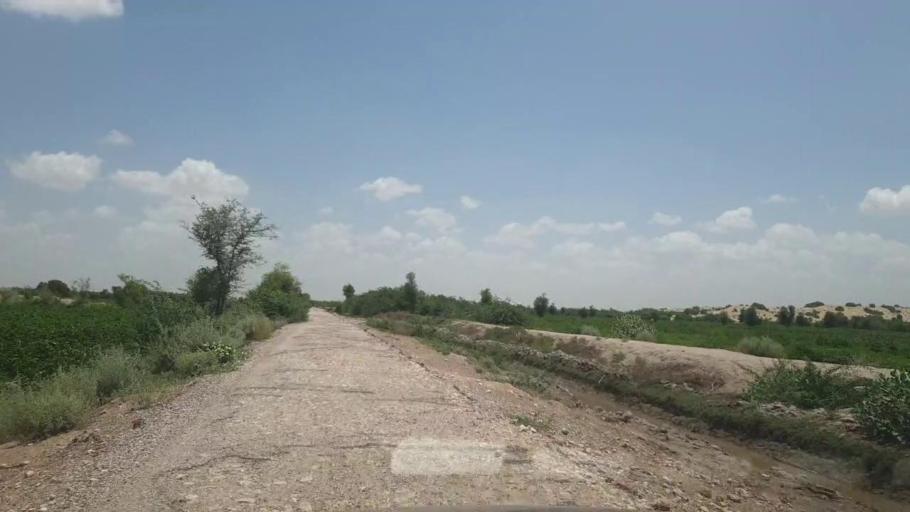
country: PK
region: Sindh
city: Kot Diji
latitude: 27.2918
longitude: 69.0851
